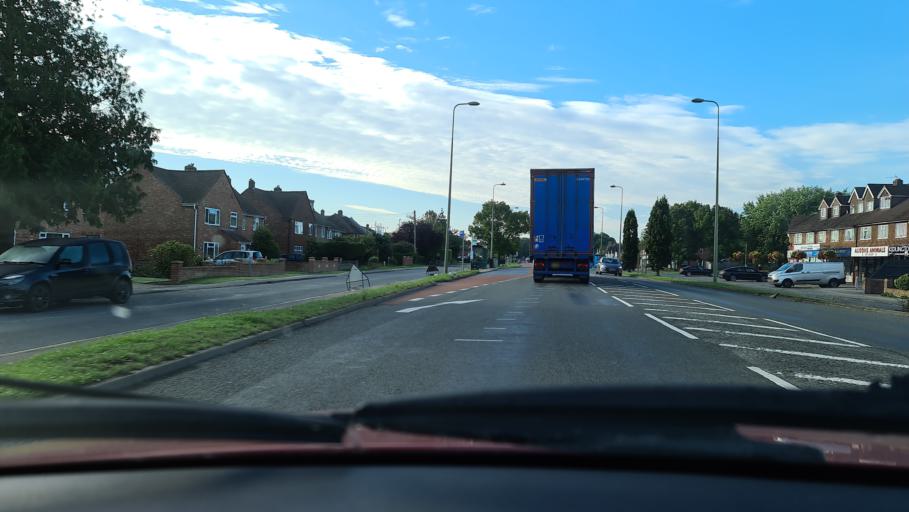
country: GB
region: England
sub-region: Oxfordshire
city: Kidlington
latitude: 51.8112
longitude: -1.2797
